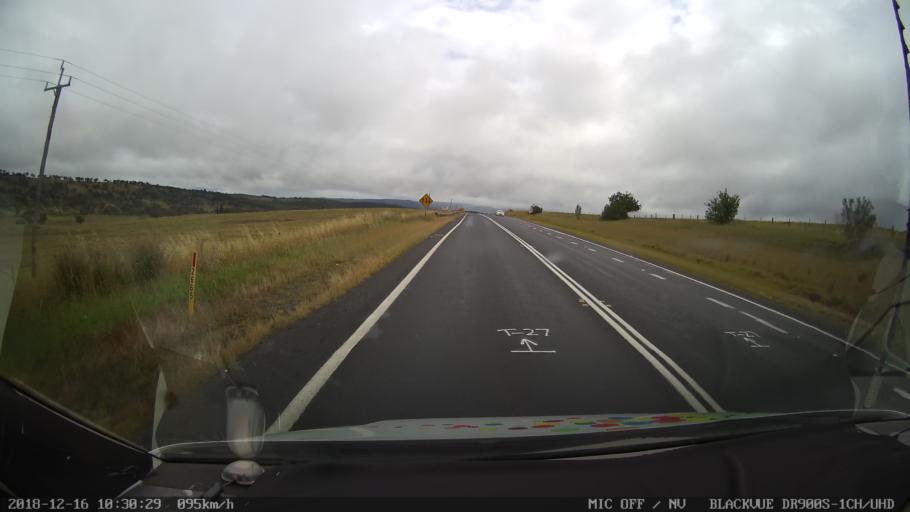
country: AU
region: New South Wales
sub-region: Tenterfield Municipality
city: Carrolls Creek
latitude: -29.0927
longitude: 152.0027
